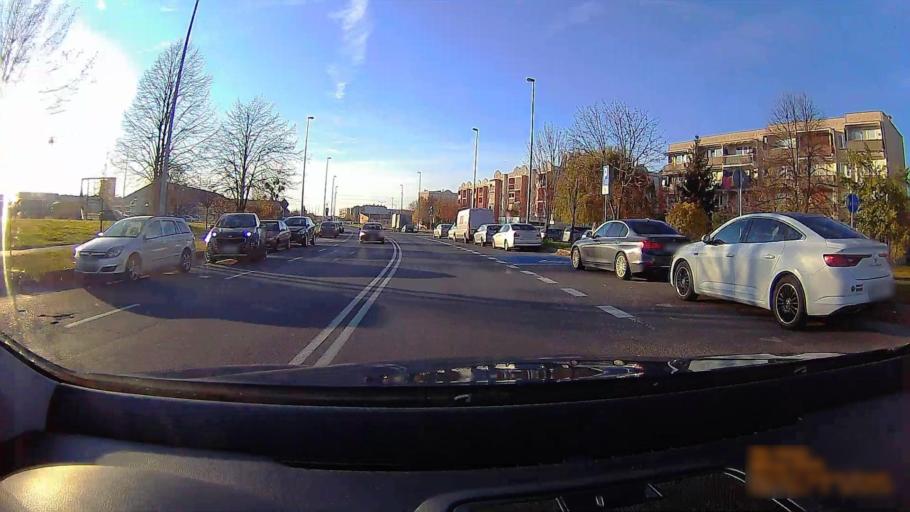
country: PL
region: Greater Poland Voivodeship
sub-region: Konin
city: Konin
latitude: 52.1980
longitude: 18.2385
